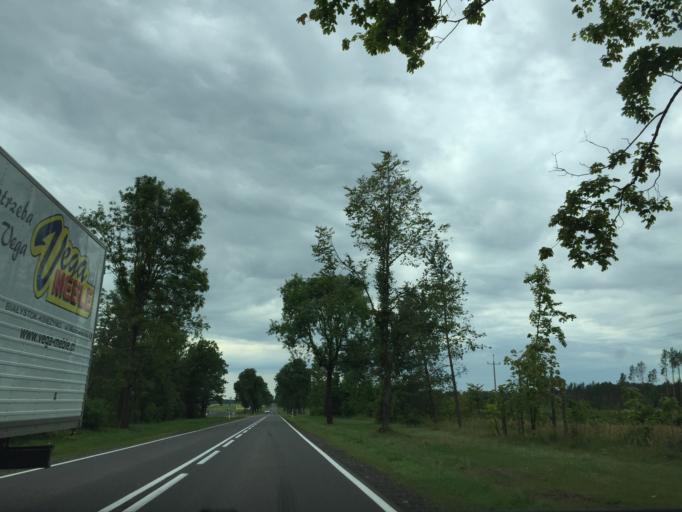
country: PL
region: Podlasie
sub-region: Powiat bielski
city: Bielsk Podlaski
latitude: 52.8964
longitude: 23.2274
